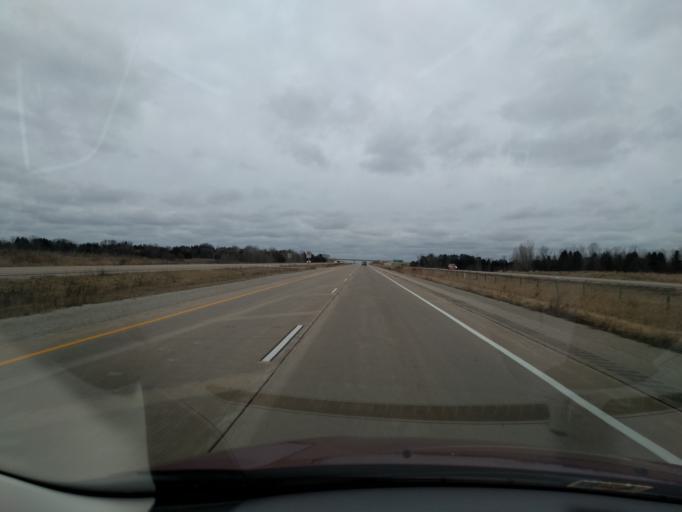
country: US
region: Wisconsin
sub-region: Winnebago County
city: Winneconne
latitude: 44.1903
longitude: -88.6716
